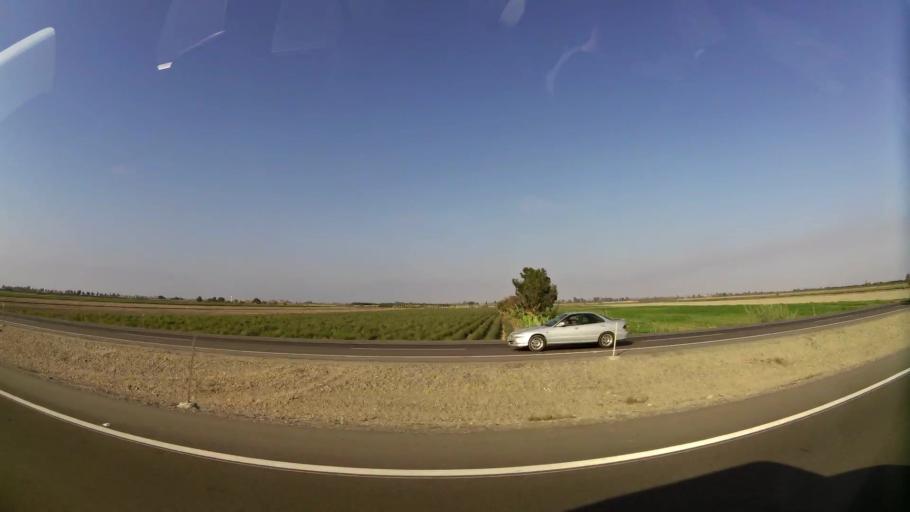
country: PE
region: Ica
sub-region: Provincia de Chincha
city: Chincha Baja
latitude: -13.5074
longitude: -76.1852
